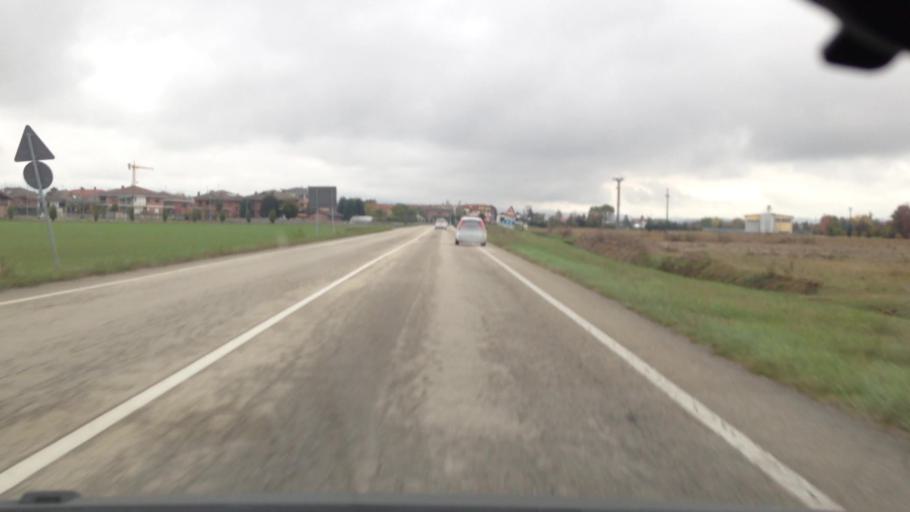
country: IT
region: Piedmont
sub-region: Provincia di Torino
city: Riva Presso Chieri
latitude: 44.9771
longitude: 7.8818
